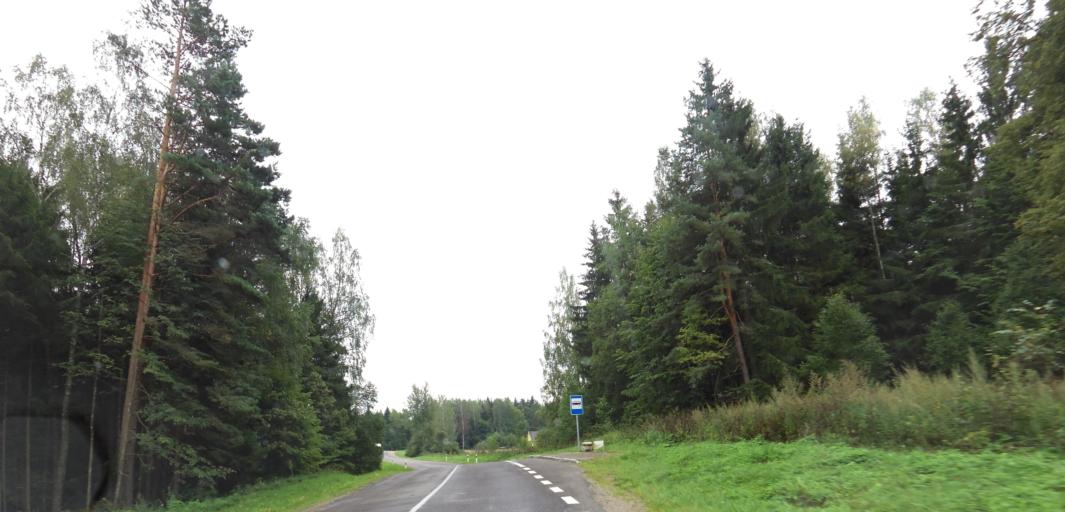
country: LT
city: Moletai
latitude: 55.3087
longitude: 25.3410
